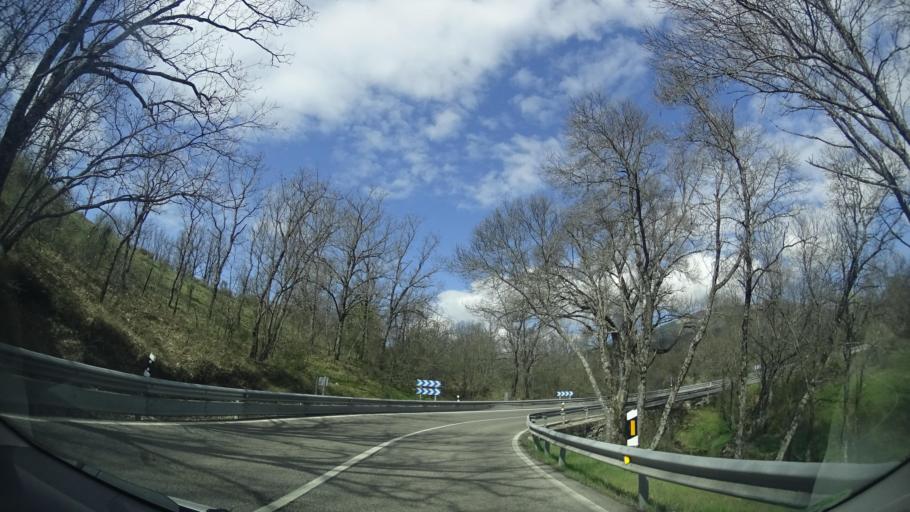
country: ES
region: Madrid
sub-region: Provincia de Madrid
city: Miraflores de la Sierra
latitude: 40.7912
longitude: -3.7754
